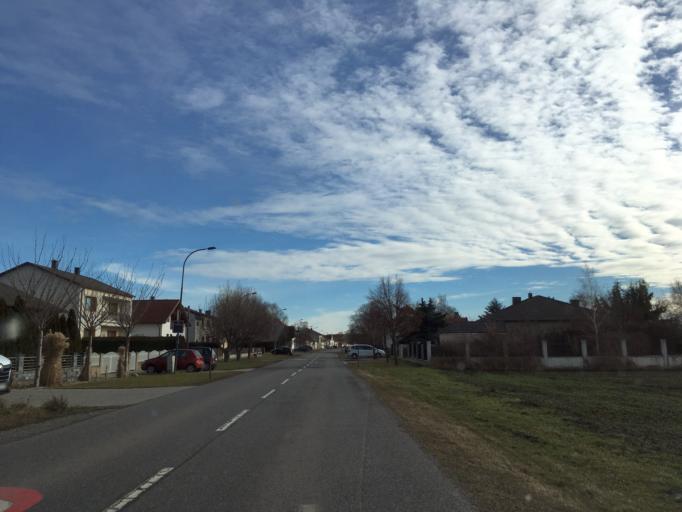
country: AT
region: Burgenland
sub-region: Politischer Bezirk Neusiedl am See
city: Pama
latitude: 48.0537
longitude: 17.0253
